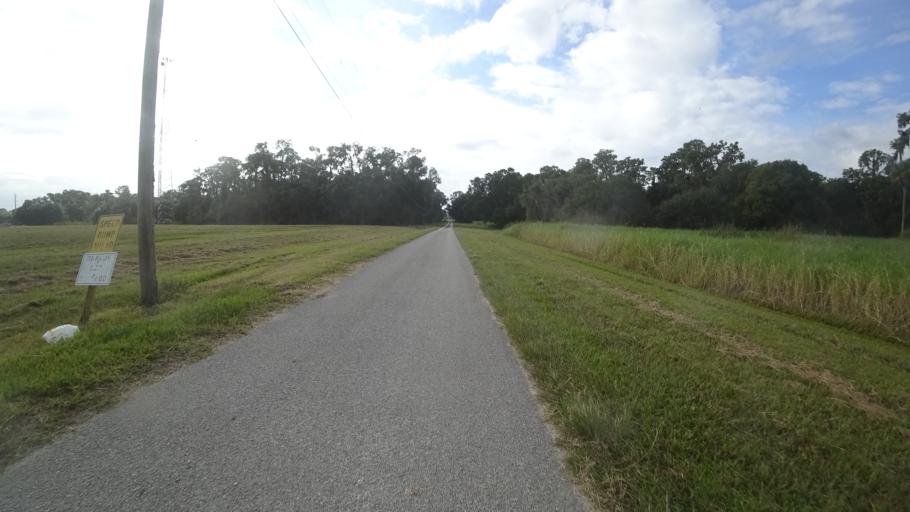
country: US
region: Florida
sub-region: Hillsborough County
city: Wimauma
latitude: 27.5956
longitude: -82.3378
